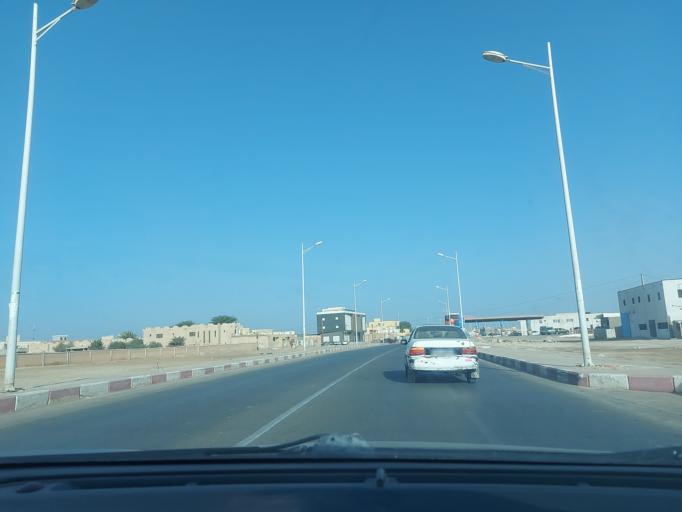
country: MR
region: Nouakchott
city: Nouakchott
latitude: 18.0844
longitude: -15.9987
